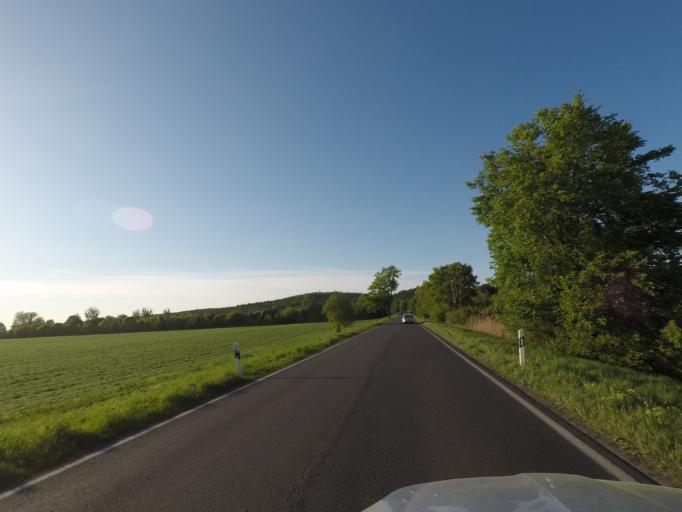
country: DE
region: Brandenburg
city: Bad Freienwalde
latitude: 52.8013
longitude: 14.0460
